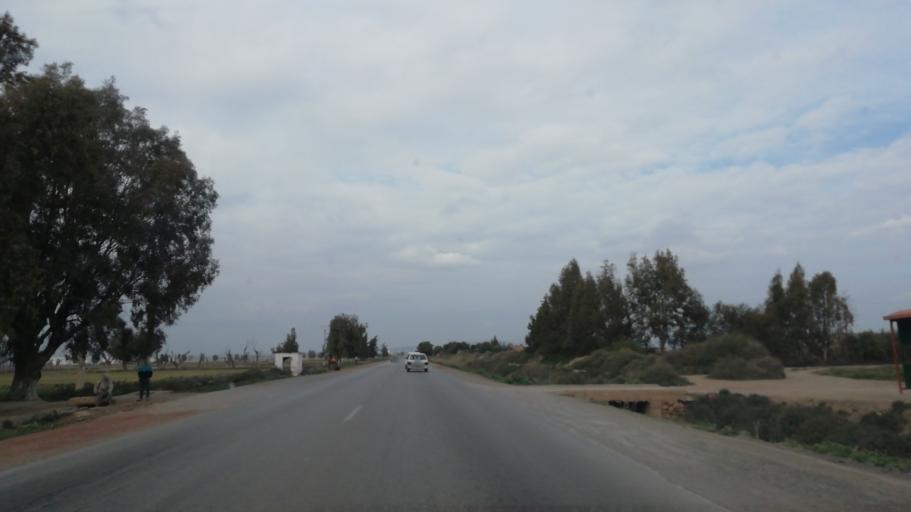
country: DZ
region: Mostaganem
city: Mostaganem
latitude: 35.6854
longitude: 0.0565
